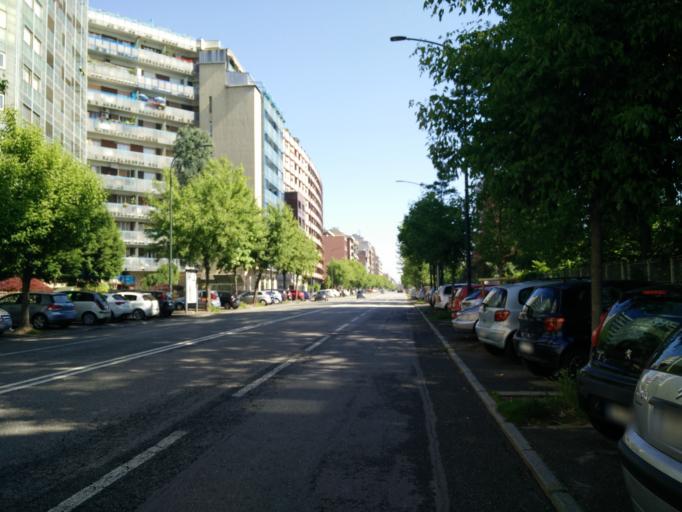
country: IT
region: Piedmont
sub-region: Provincia di Torino
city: Moncalieri
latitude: 45.0194
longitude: 7.6661
